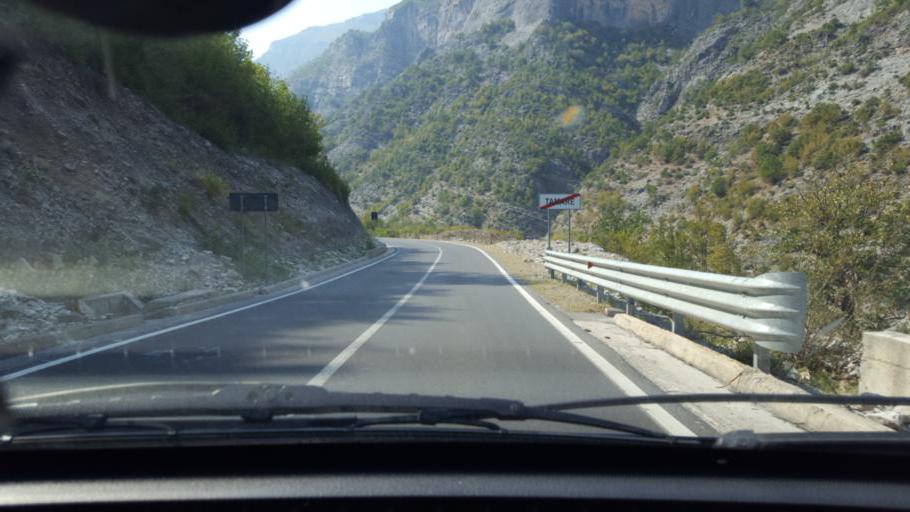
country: AL
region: Shkoder
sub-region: Rrethi i Malesia e Madhe
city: Kastrat
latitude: 42.4530
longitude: 19.5539
